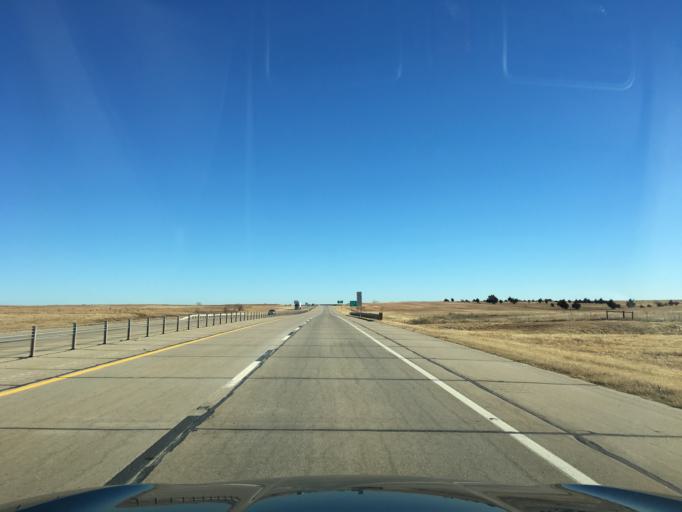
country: US
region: Oklahoma
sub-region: Noble County
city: Perry
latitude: 36.4000
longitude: -97.3128
